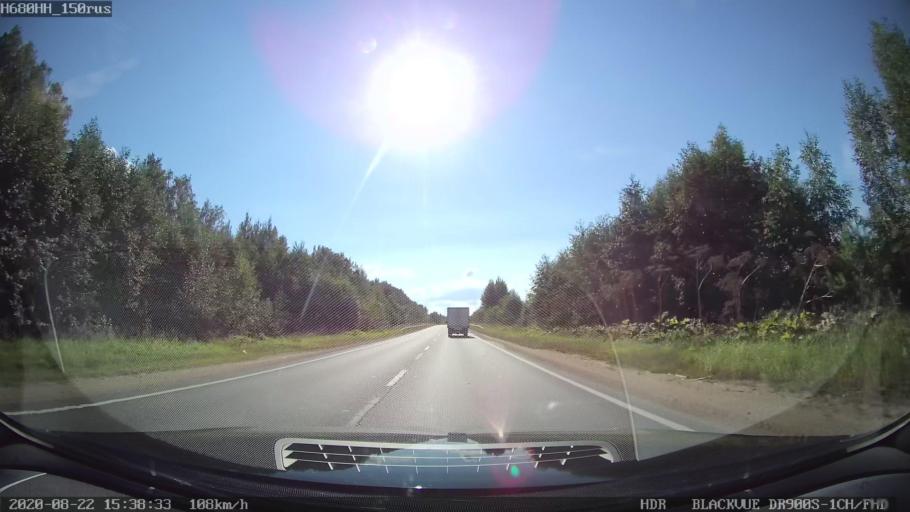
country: RU
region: Tverskaya
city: Bezhetsk
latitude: 57.7615
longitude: 36.6453
